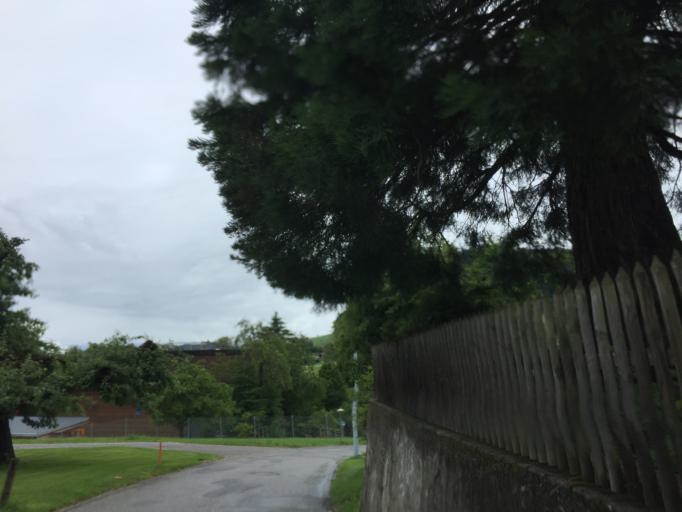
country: CH
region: Bern
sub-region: Bern-Mittelland District
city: Zaziwil
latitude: 46.9004
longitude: 7.6387
